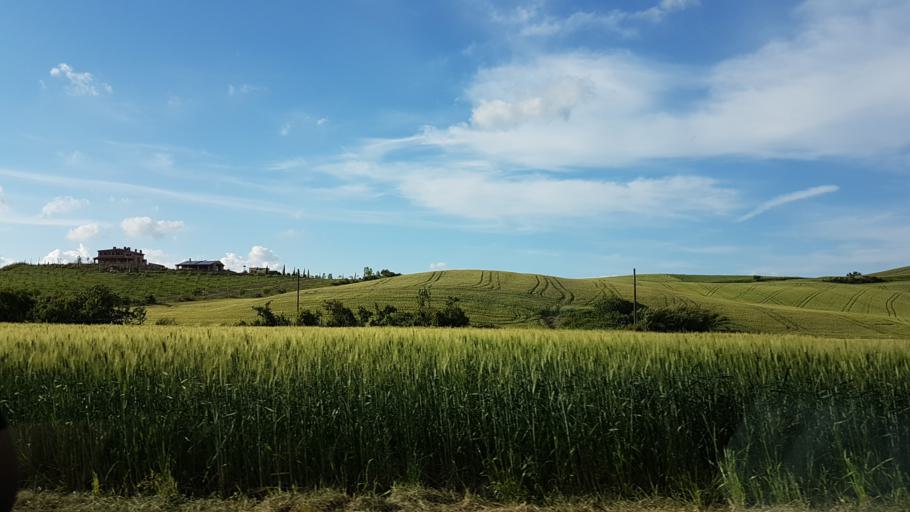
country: IT
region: Tuscany
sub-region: Province of Pisa
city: Chianni
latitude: 43.4813
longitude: 10.6808
